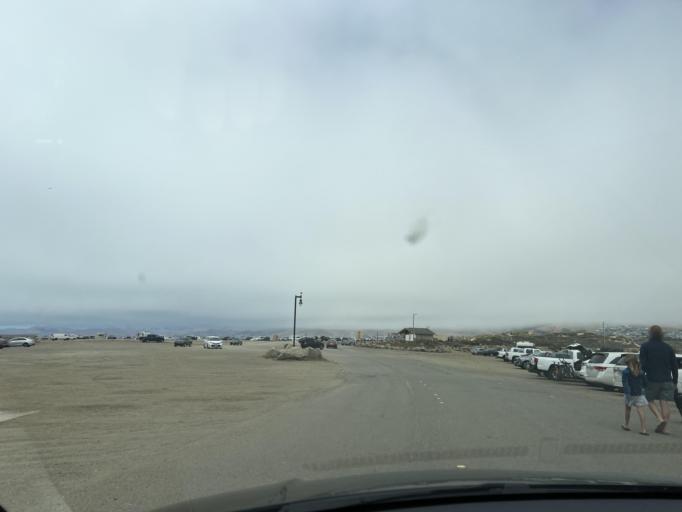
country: US
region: California
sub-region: San Luis Obispo County
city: Morro Bay
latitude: 35.3692
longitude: -120.8648
